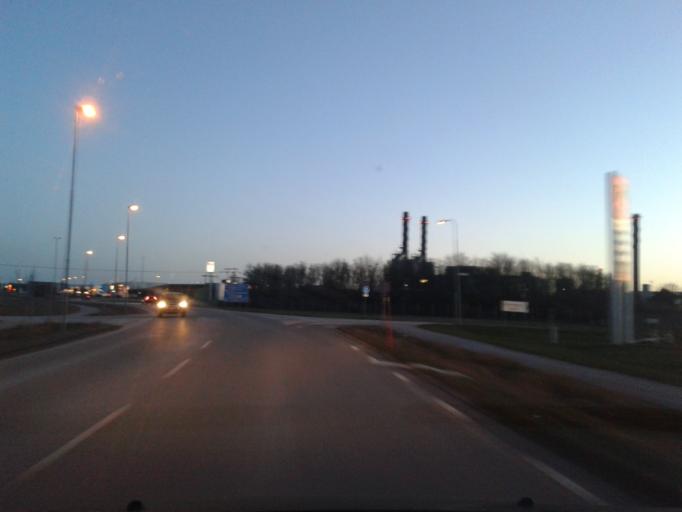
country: SE
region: Gotland
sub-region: Gotland
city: Visby
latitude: 57.6266
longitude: 18.3185
